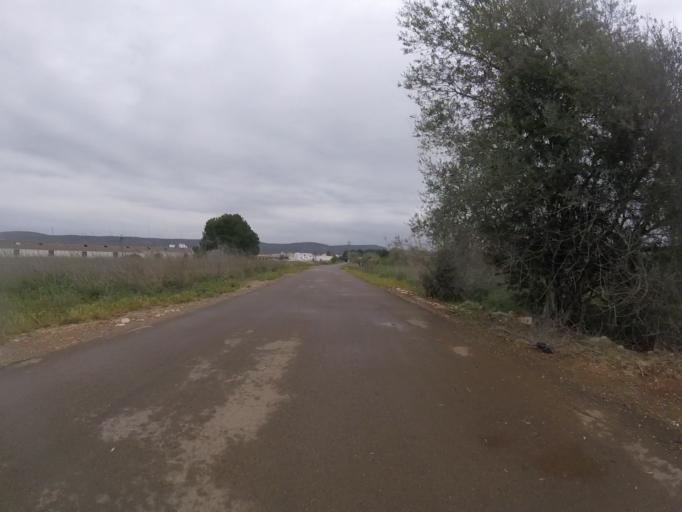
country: ES
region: Valencia
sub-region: Provincia de Castello
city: Alcala de Xivert
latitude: 40.2953
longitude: 0.2284
